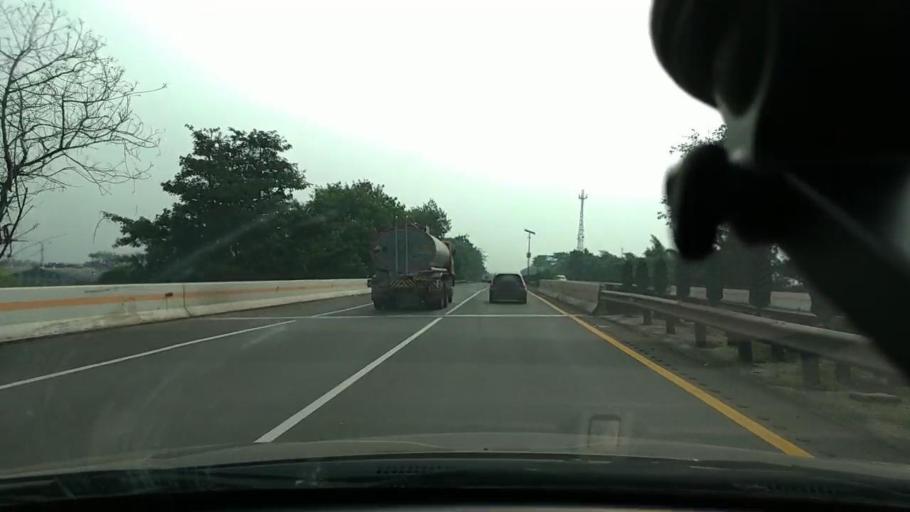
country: ID
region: Banten
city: Serang
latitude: -6.0929
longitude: 106.1580
